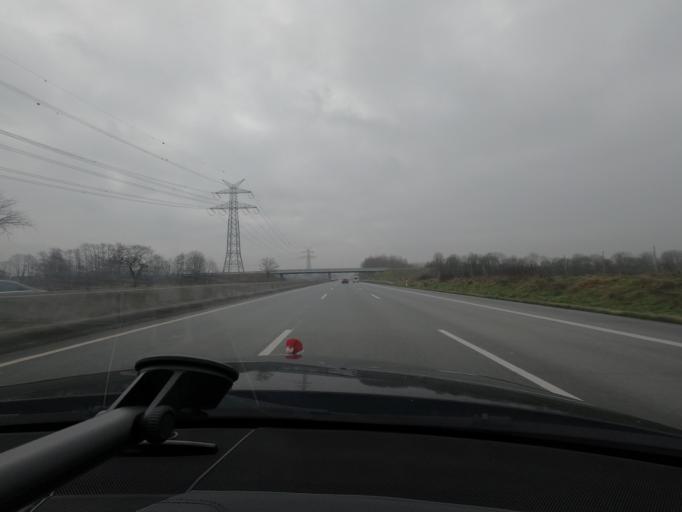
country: DE
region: Schleswig-Holstein
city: Alveslohe
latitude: 53.7754
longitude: 9.9436
